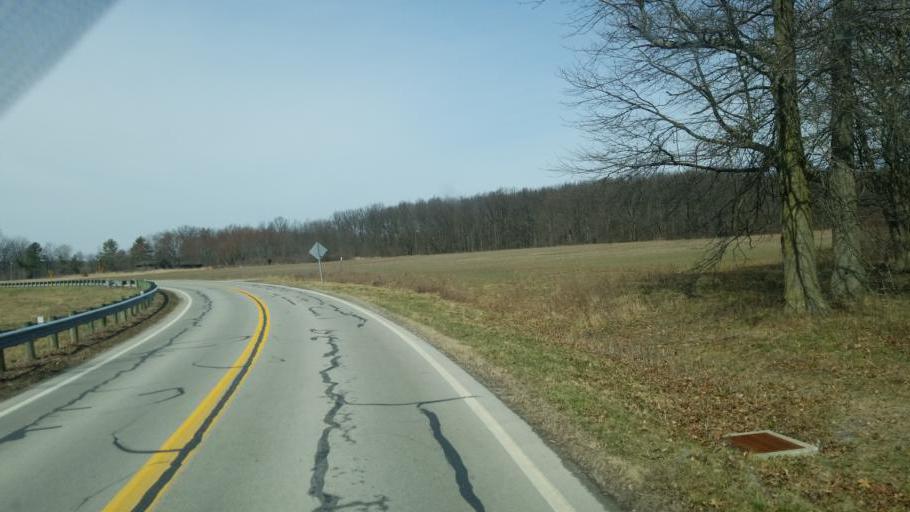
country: US
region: Ohio
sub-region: Lorain County
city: Vermilion-on-the-Lake
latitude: 41.3838
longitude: -82.3134
